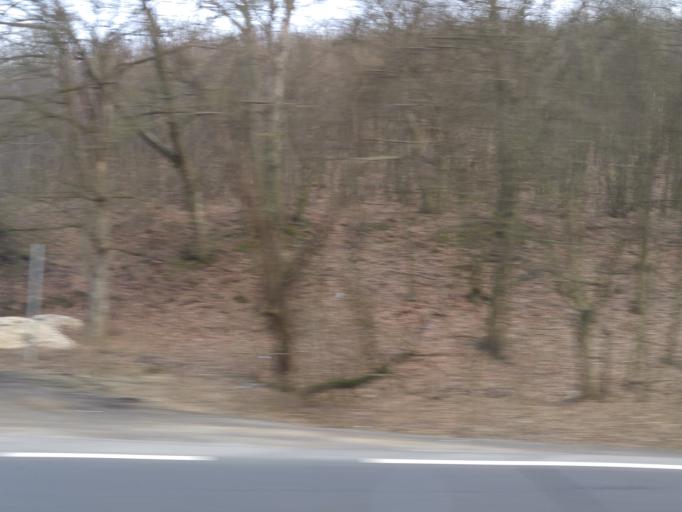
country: HU
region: Nograd
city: Retsag
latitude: 47.8657
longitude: 19.1085
